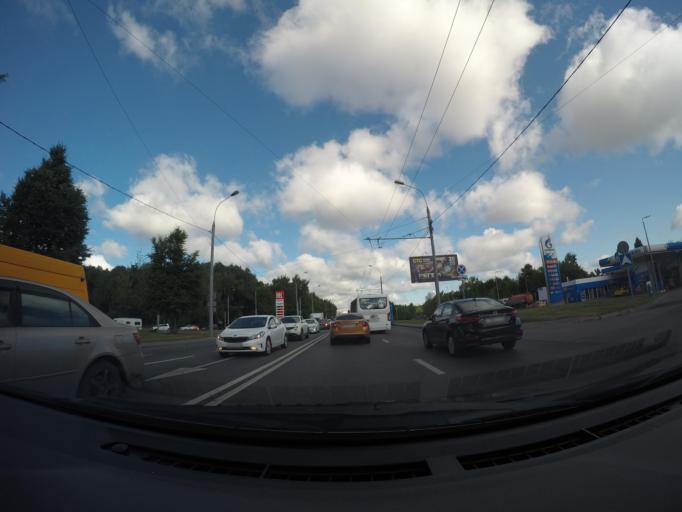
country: RU
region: Moscow
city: Khimki
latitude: 55.8717
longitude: 37.4408
